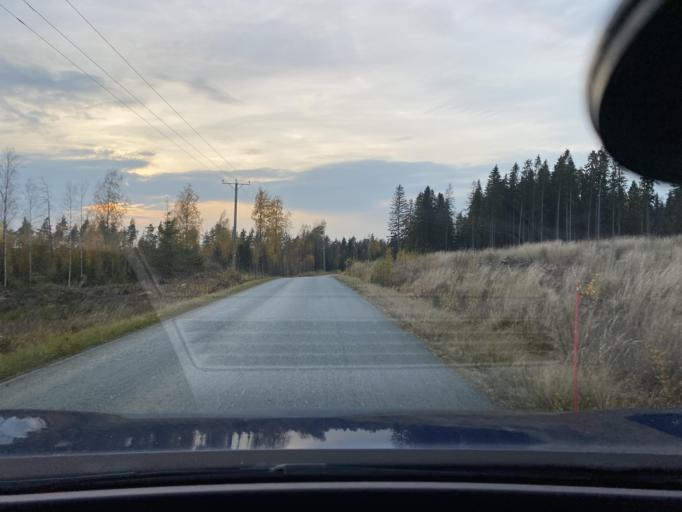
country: FI
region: Varsinais-Suomi
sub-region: Loimaa
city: Alastaro
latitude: 61.0830
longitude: 22.9374
